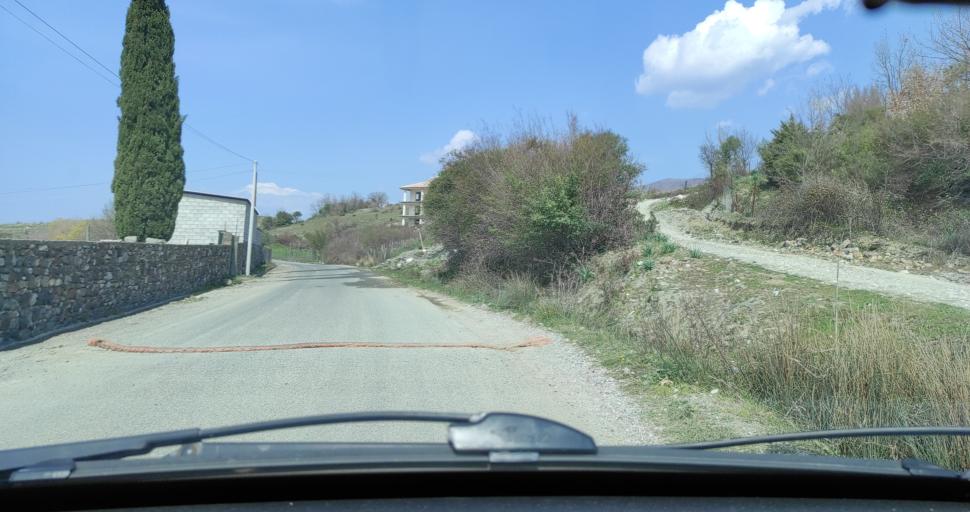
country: AL
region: Lezhe
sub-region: Rrethi i Lezhes
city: Kallmeti i Madh
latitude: 41.8613
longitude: 19.6990
